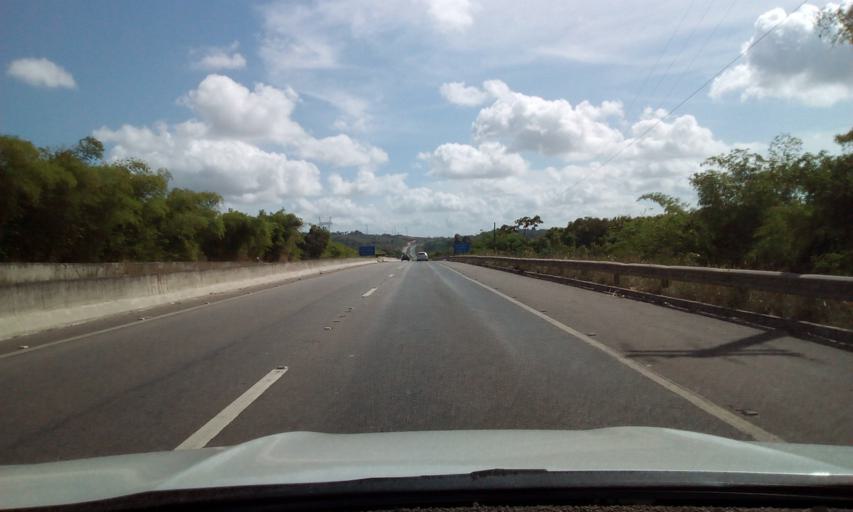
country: BR
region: Paraiba
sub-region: Conde
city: Conde
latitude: -7.2072
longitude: -34.9094
